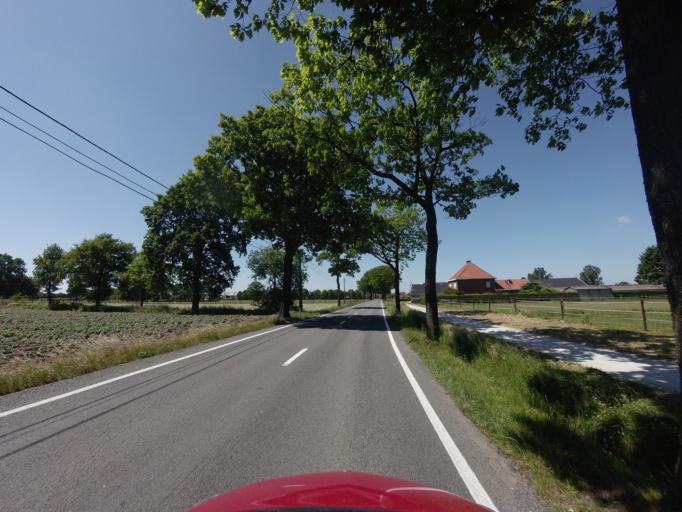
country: BE
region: Flanders
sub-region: Provincie Antwerpen
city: Ravels
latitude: 51.3821
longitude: 5.0211
